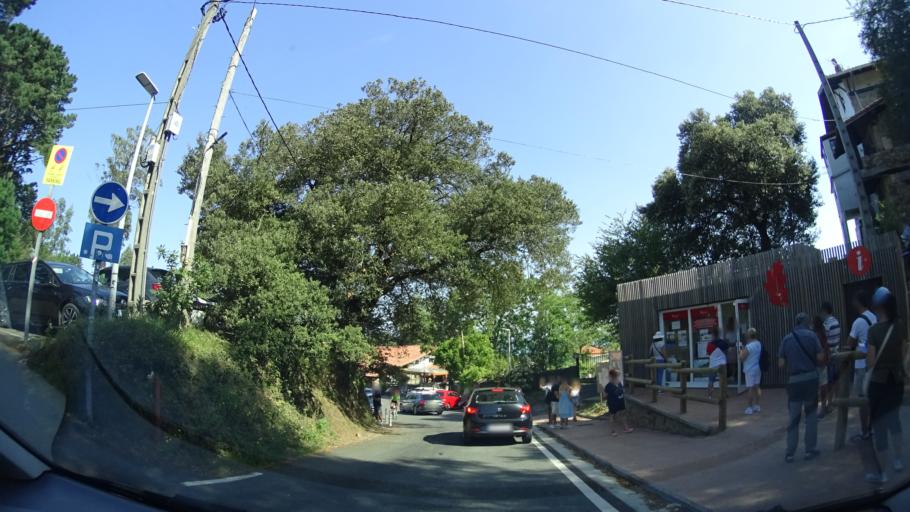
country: ES
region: Basque Country
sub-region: Bizkaia
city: Bakio
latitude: 43.4403
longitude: -2.7833
